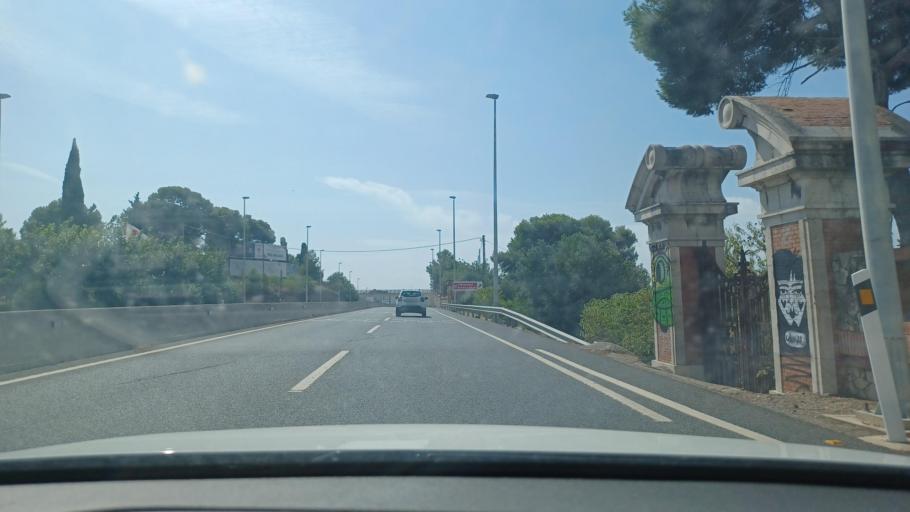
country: ES
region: Catalonia
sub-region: Provincia de Tarragona
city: Tarragona
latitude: 41.1334
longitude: 1.2388
